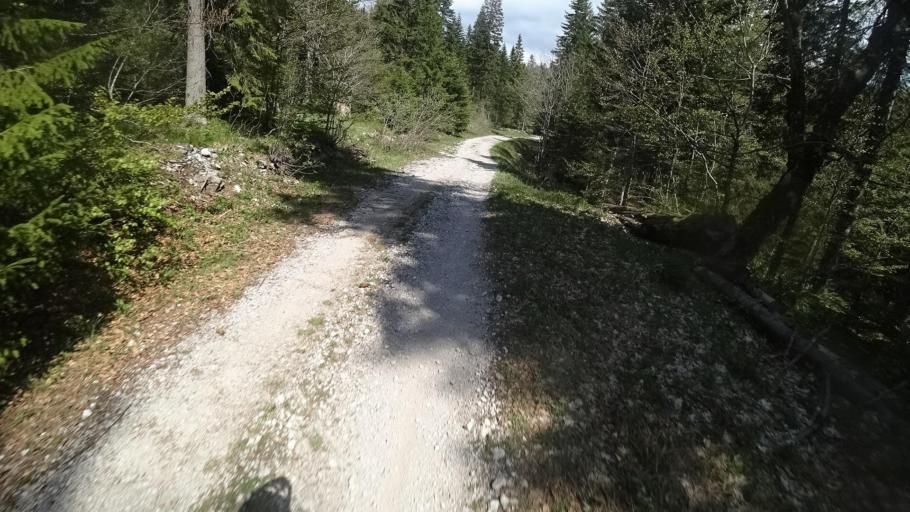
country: BA
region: Republika Srpska
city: Sipovo
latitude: 44.1407
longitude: 17.0140
